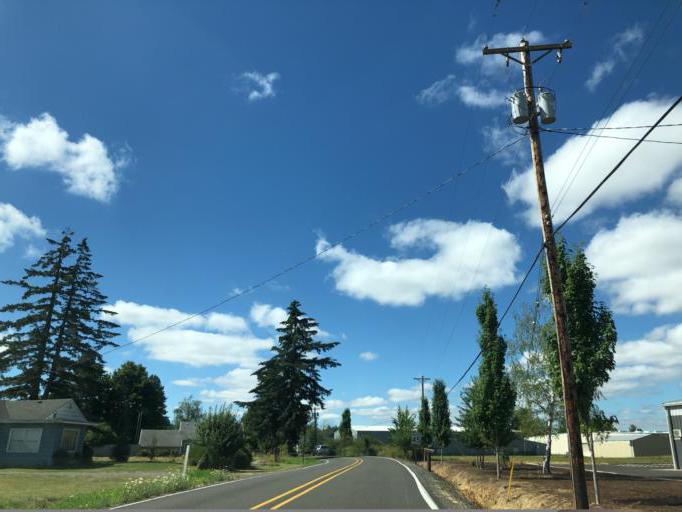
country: US
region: Oregon
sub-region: Marion County
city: Silverton
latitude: 45.0215
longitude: -122.7683
